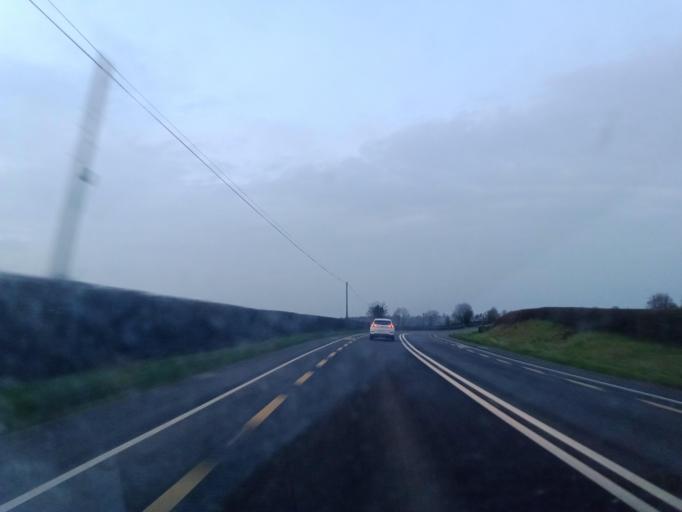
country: IE
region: Leinster
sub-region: Laois
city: Abbeyleix
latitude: 52.8644
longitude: -7.3687
